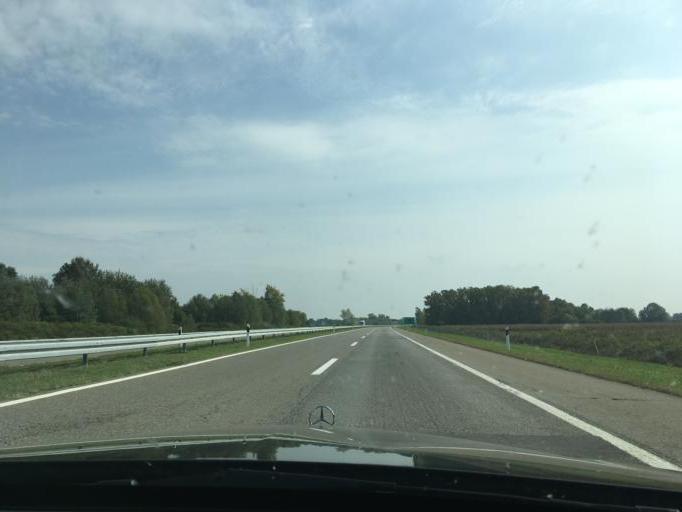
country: HR
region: Vukovarsko-Srijemska
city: Stitar
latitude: 45.1117
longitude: 18.5686
